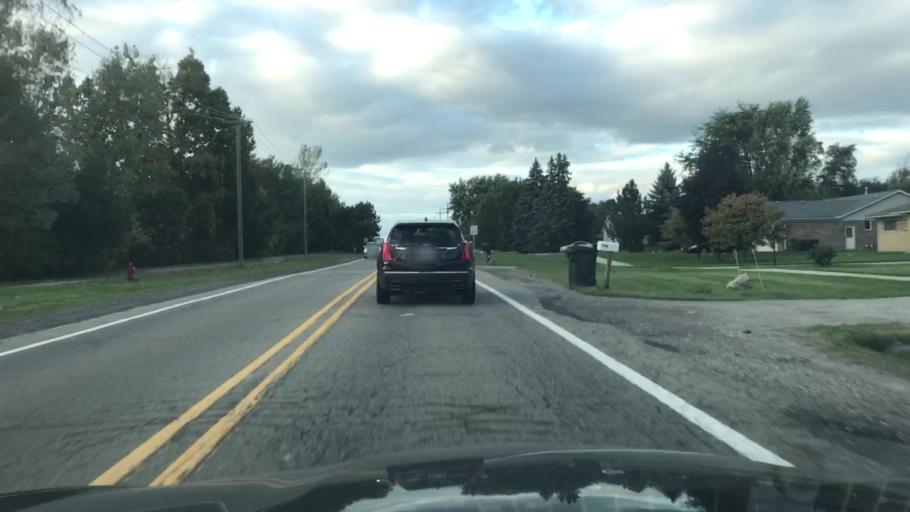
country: US
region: Michigan
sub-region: Oakland County
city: Rochester
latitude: 42.6836
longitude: -83.0942
